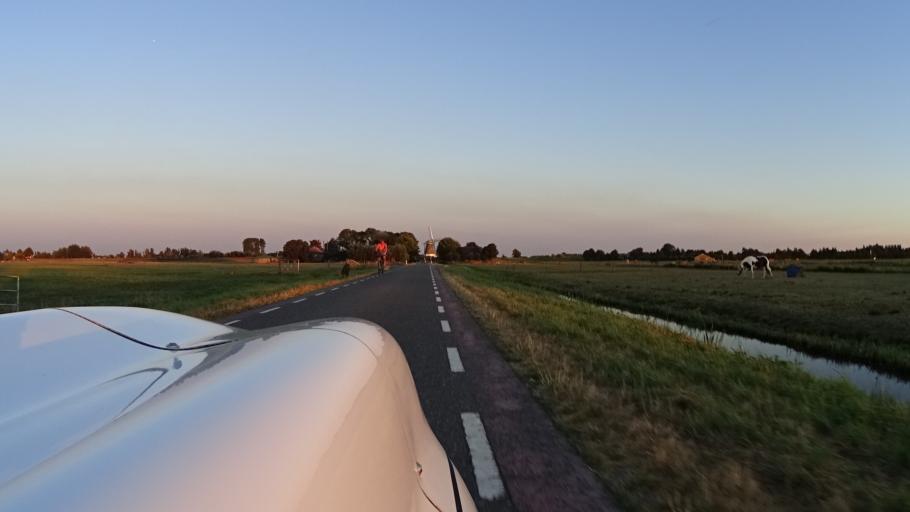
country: NL
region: South Holland
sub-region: Gemeente Kaag en Braassem
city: Oude Wetering
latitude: 52.1834
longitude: 4.6189
